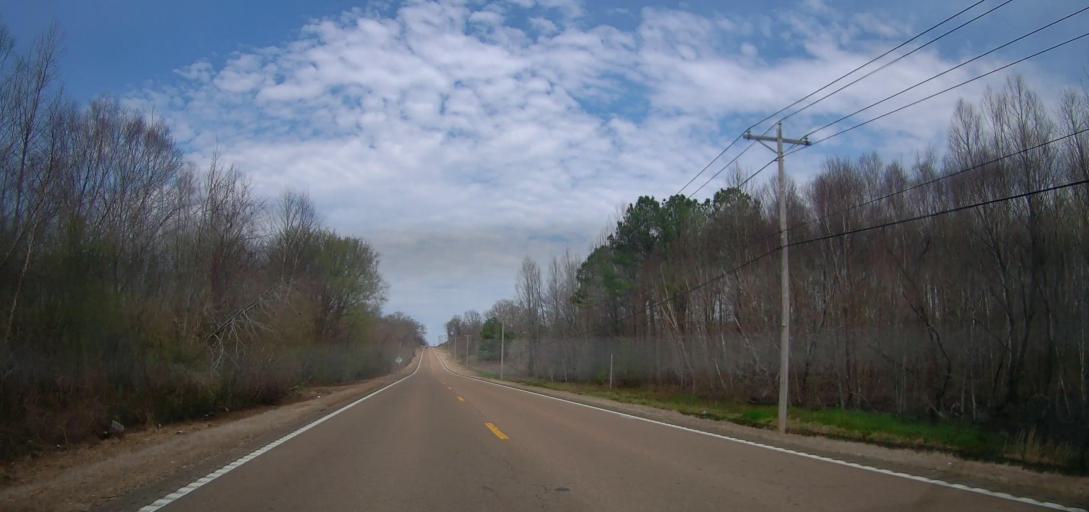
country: US
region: Mississippi
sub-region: Marshall County
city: Holly Springs
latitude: 34.7309
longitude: -89.4199
